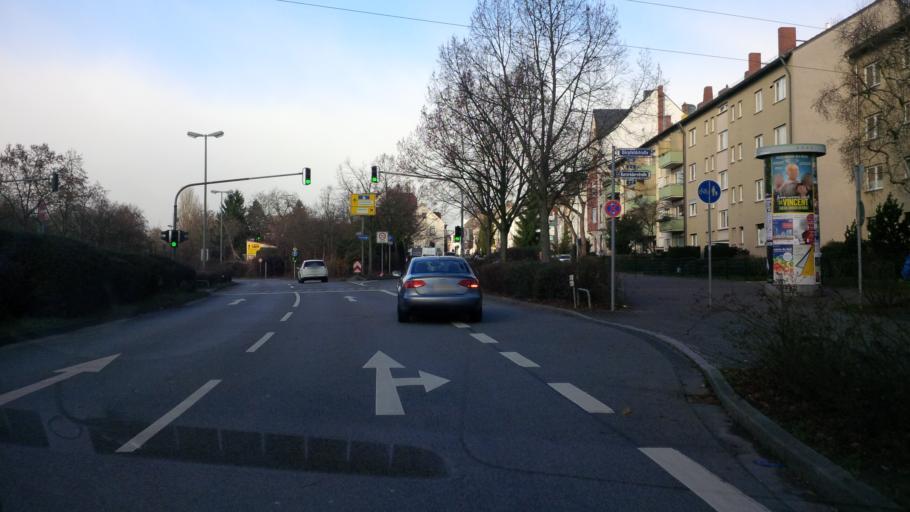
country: DE
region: Hesse
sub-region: Regierungsbezirk Darmstadt
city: Frankfurt am Main
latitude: 50.1439
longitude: 8.6831
